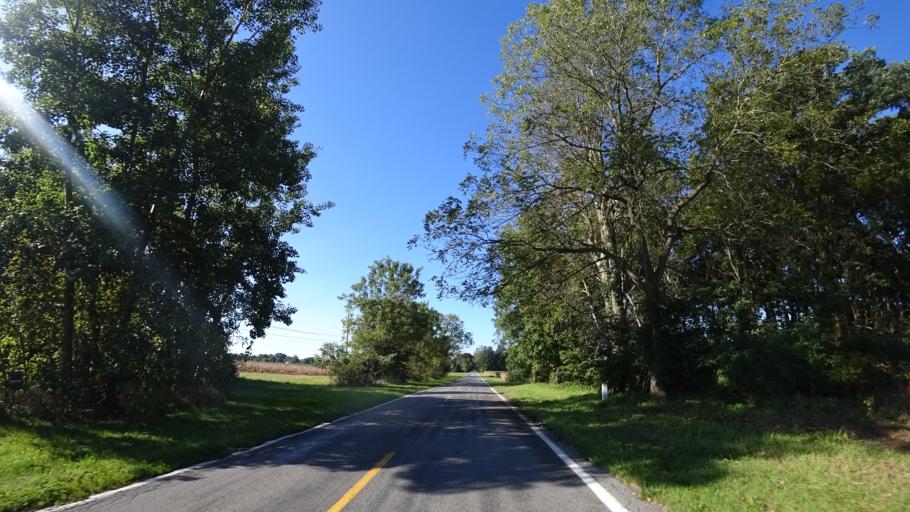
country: US
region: Michigan
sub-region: Berrien County
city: Benton Heights
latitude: 42.1701
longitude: -86.3937
